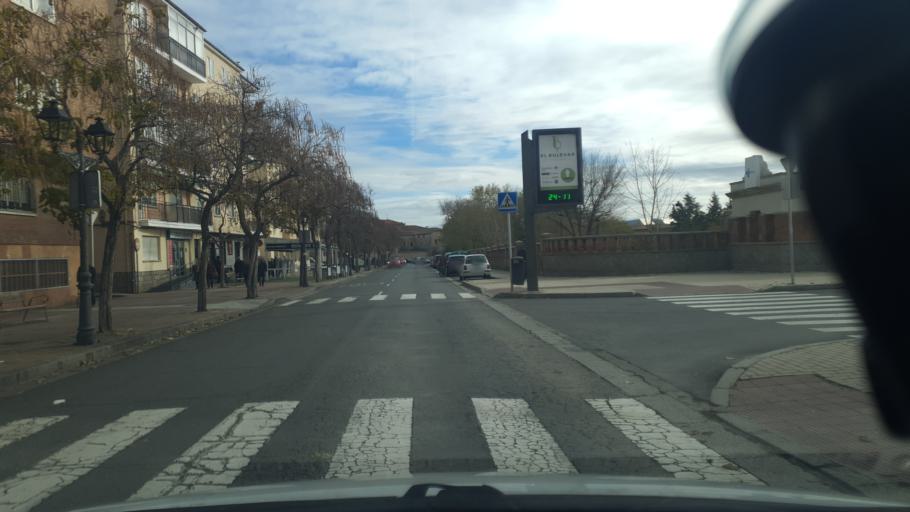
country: ES
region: Castille and Leon
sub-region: Provincia de Avila
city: Avila
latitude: 40.6511
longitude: -4.6921
